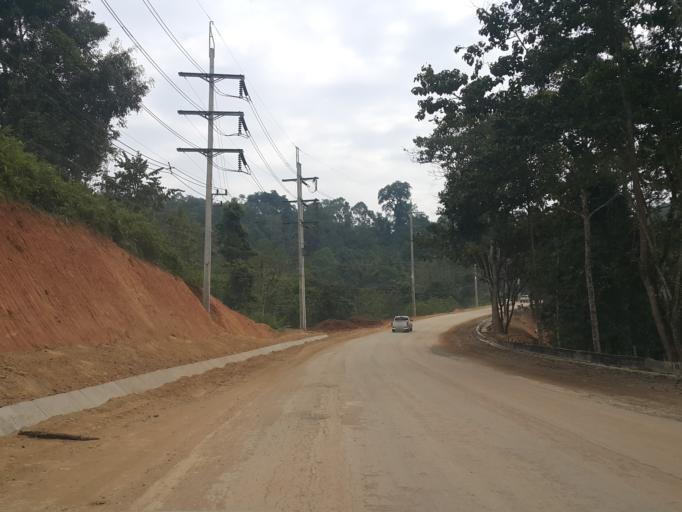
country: TH
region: Chiang Mai
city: Mae Taeng
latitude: 19.1421
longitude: 98.6982
